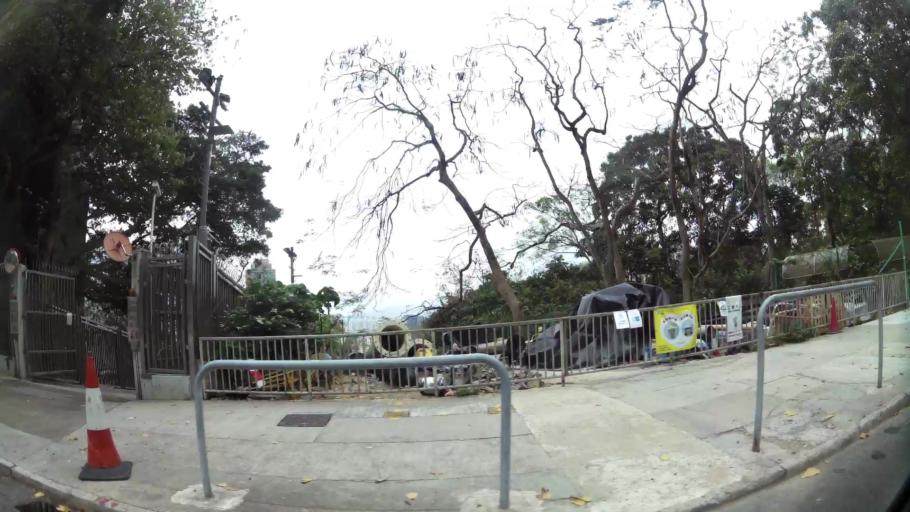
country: HK
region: Wong Tai Sin
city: Wong Tai Sin
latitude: 22.3498
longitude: 114.1961
